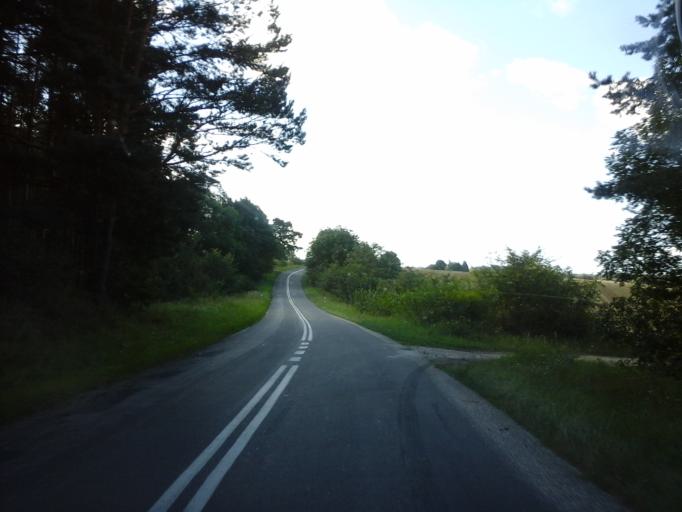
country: PL
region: West Pomeranian Voivodeship
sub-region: Powiat stargardzki
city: Suchan
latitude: 53.2197
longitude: 15.2922
